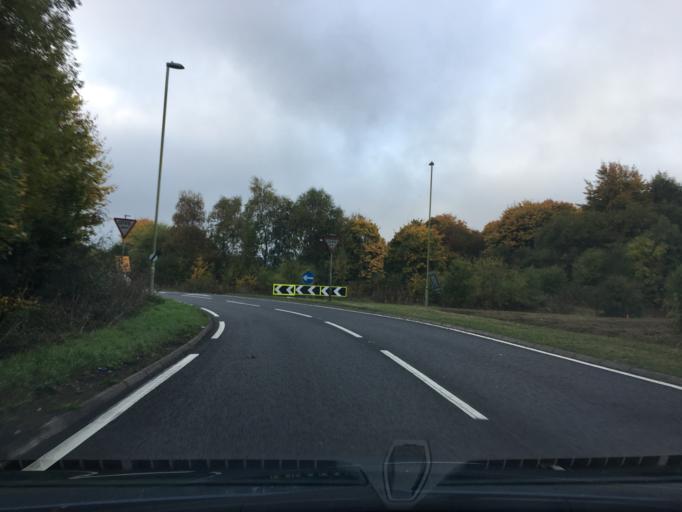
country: GB
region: England
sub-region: Hampshire
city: Alton
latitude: 51.1579
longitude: -0.9490
